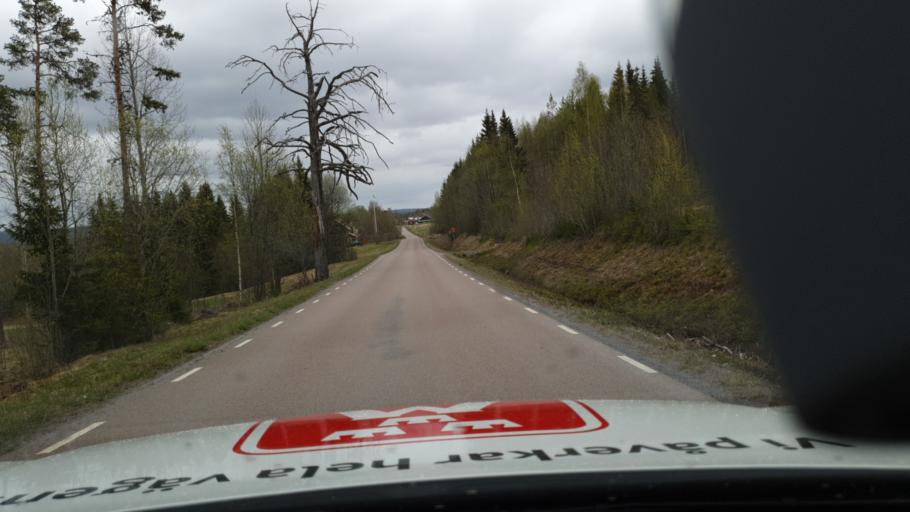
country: SE
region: Jaemtland
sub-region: OEstersunds Kommun
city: Lit
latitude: 63.3039
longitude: 14.9372
